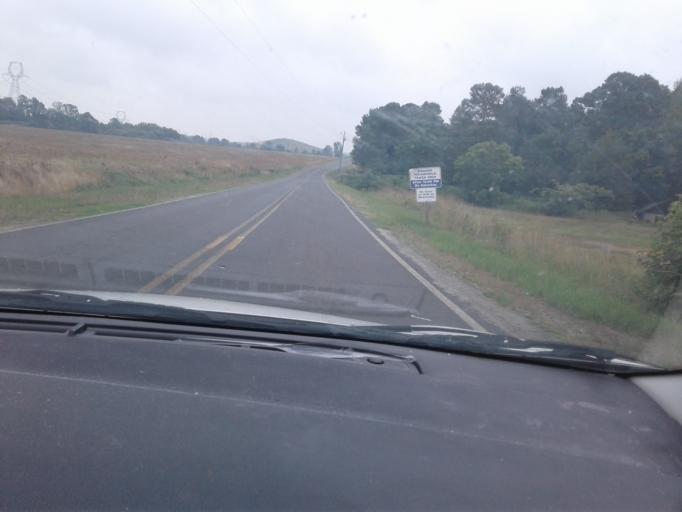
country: US
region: North Carolina
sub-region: Harnett County
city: Coats
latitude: 35.3759
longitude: -78.6475
